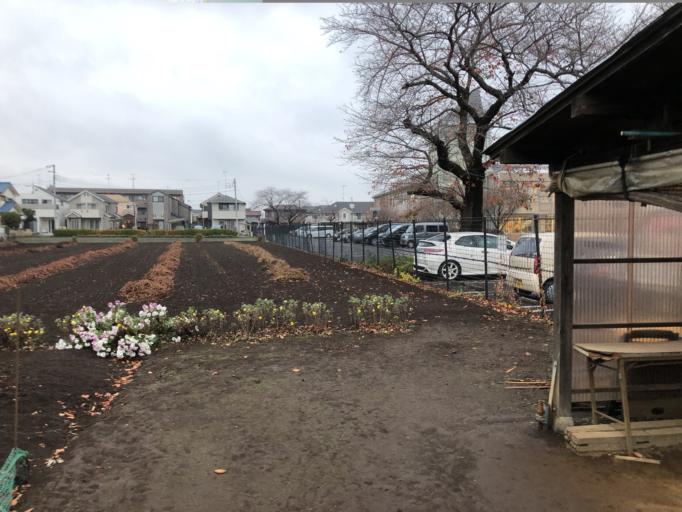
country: JP
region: Tokyo
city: Tanashicho
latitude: 35.7754
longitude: 139.5309
